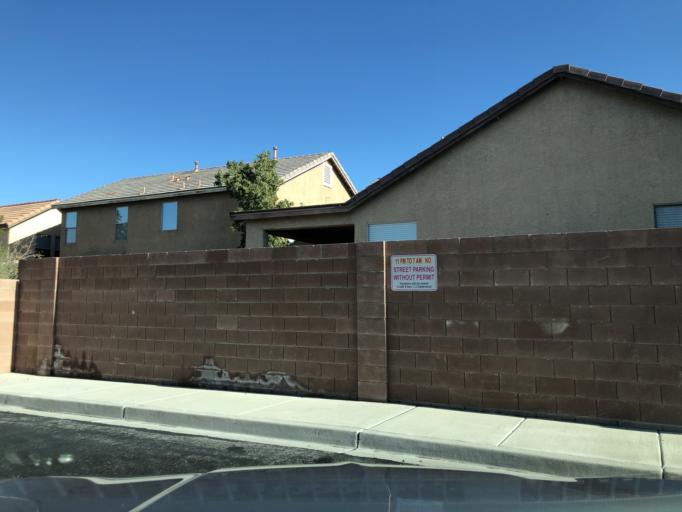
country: US
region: Nevada
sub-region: Clark County
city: Whitney
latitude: 35.9990
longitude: -115.0924
